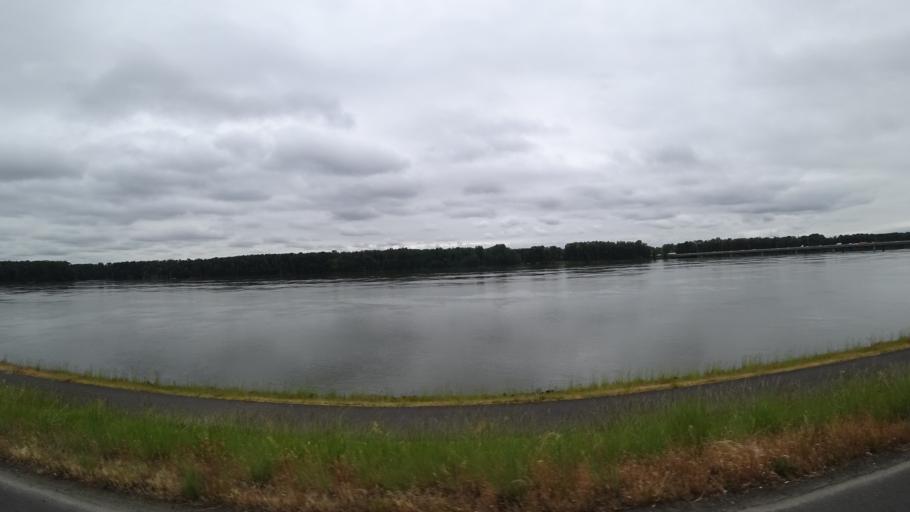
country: US
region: Washington
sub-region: Clark County
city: Orchards
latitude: 45.5786
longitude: -122.5550
